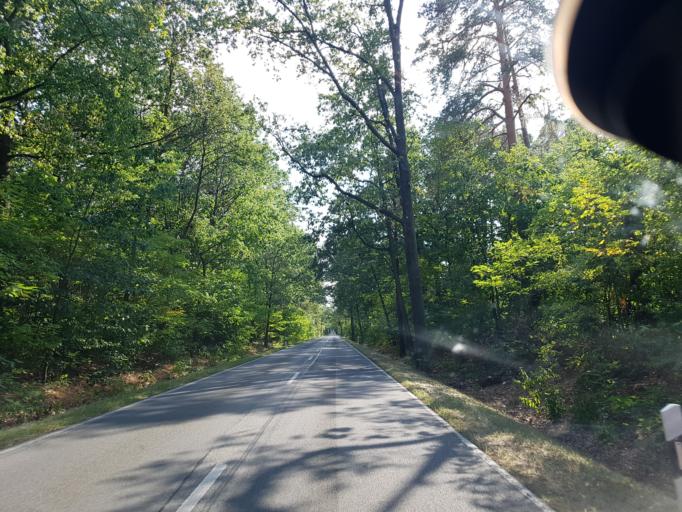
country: DE
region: Brandenburg
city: Calau
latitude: 51.7696
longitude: 13.9501
